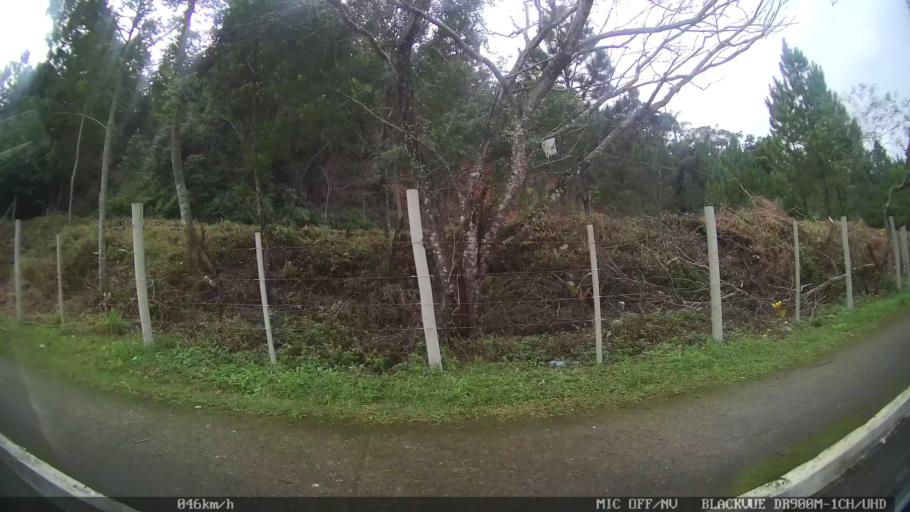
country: BR
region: Santa Catarina
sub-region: Sao Jose
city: Campinas
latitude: -27.5540
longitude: -48.6434
